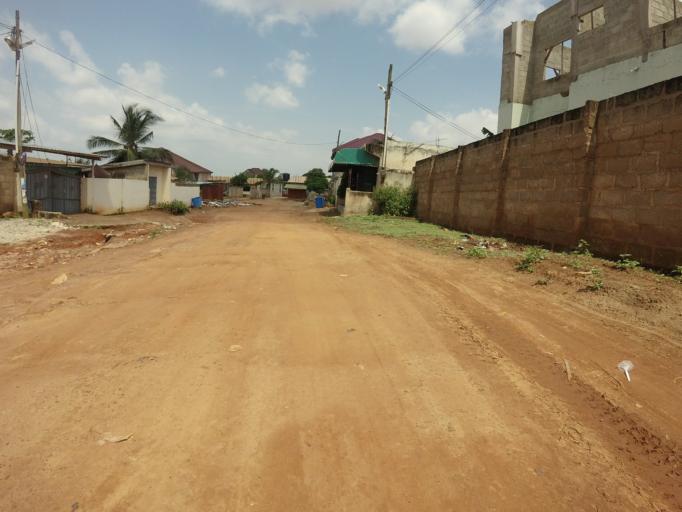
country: GH
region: Greater Accra
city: Gbawe
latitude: 5.6182
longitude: -0.3121
